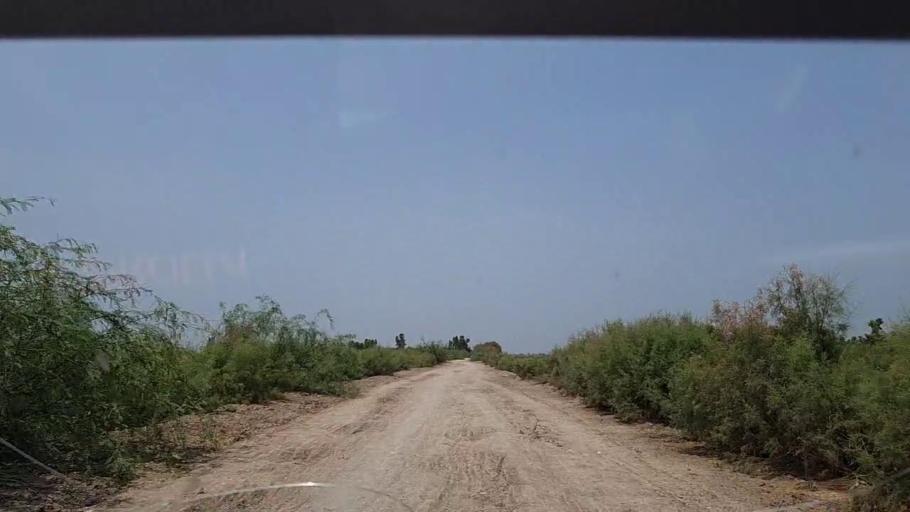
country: PK
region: Sindh
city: Adilpur
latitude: 27.9007
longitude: 69.2322
